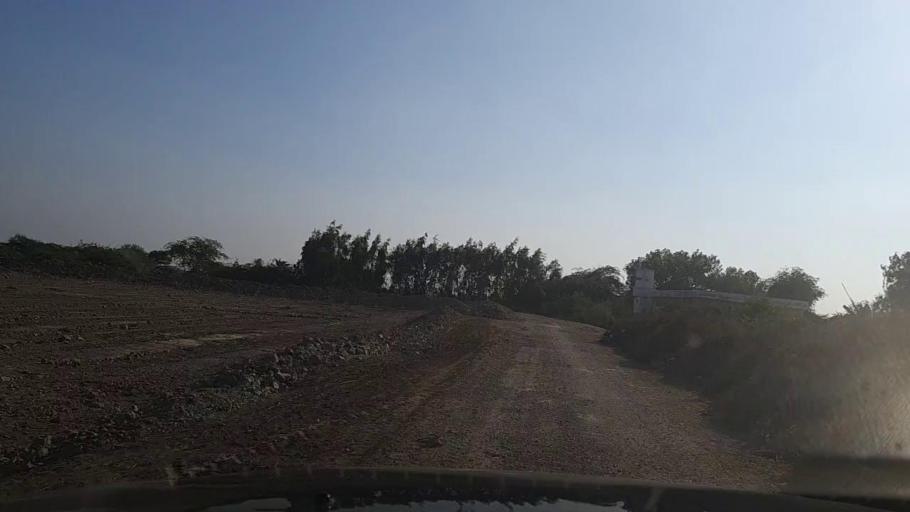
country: PK
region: Sindh
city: Gharo
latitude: 24.7046
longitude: 67.7046
